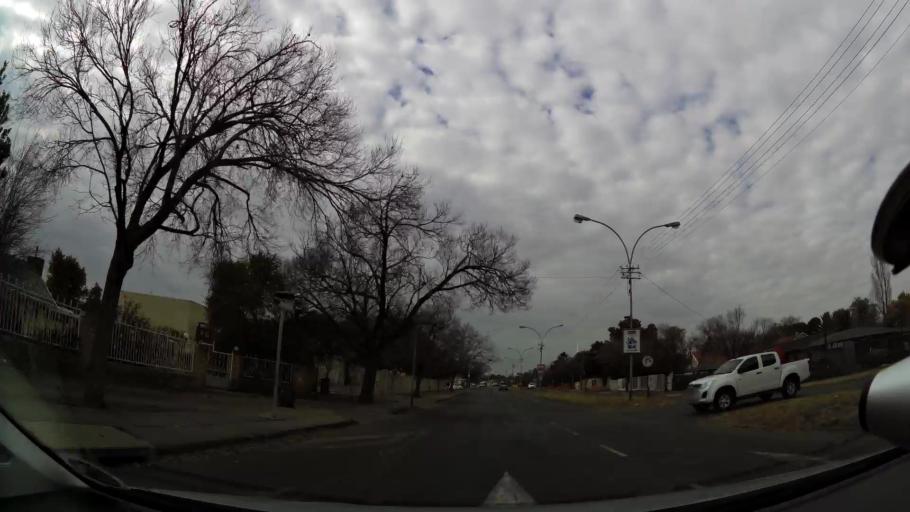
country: ZA
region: Orange Free State
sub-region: Mangaung Metropolitan Municipality
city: Bloemfontein
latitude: -29.0895
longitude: 26.2114
